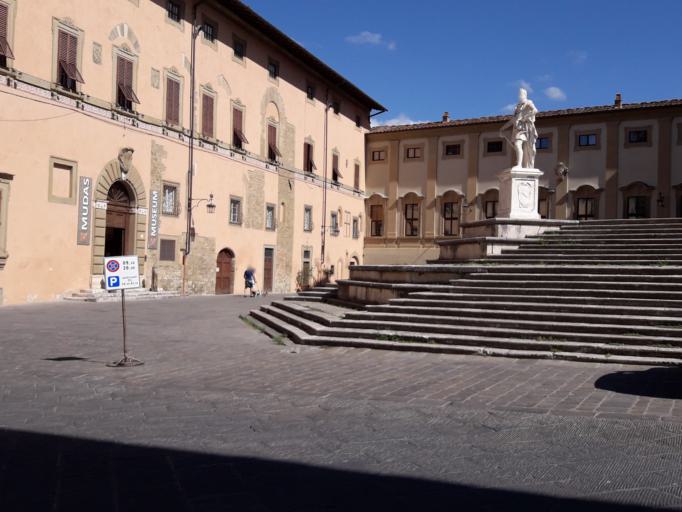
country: IT
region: Tuscany
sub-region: Province of Arezzo
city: Arezzo
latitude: 43.4667
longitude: 11.8827
